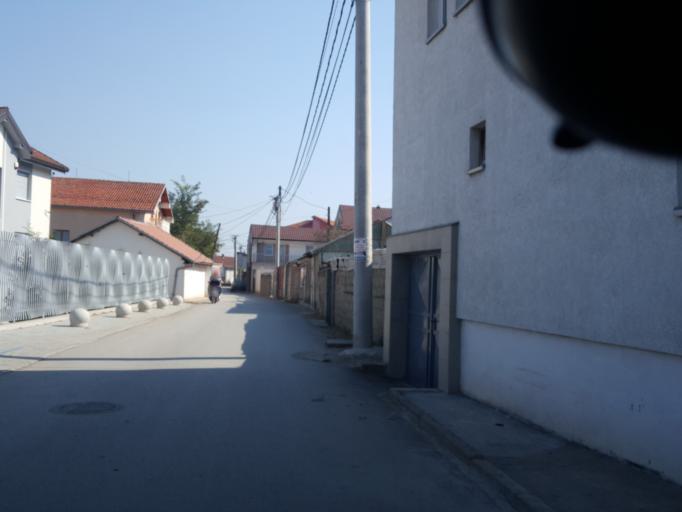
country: XK
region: Gjakova
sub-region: Komuna e Gjakoves
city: Gjakove
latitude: 42.3906
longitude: 20.4201
